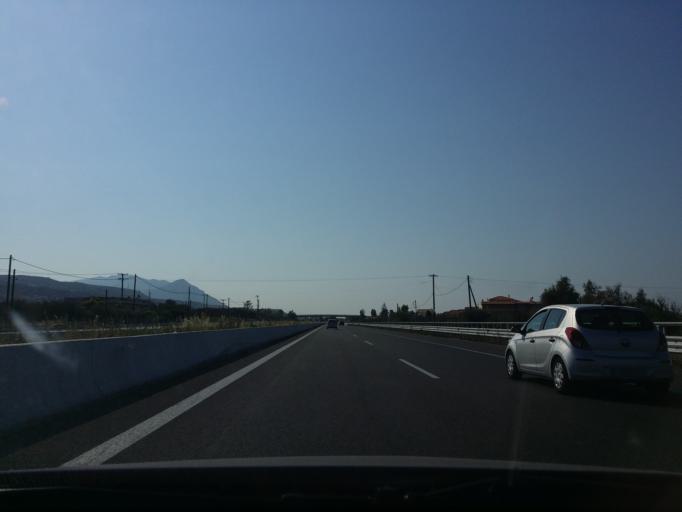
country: GR
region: Peloponnese
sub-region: Nomos Korinthias
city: Xylokastro
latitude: 38.0532
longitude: 22.6774
